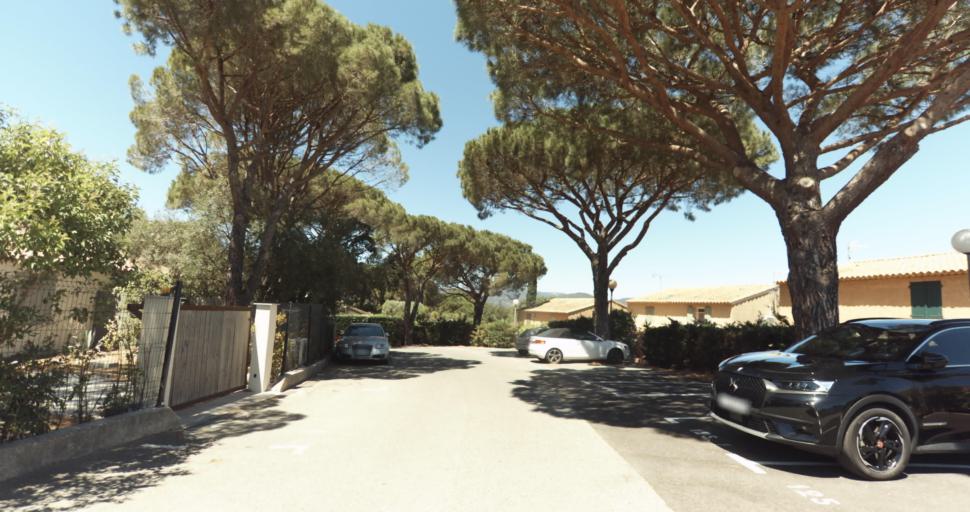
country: FR
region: Provence-Alpes-Cote d'Azur
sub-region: Departement du Var
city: Gassin
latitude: 43.2594
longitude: 6.5732
